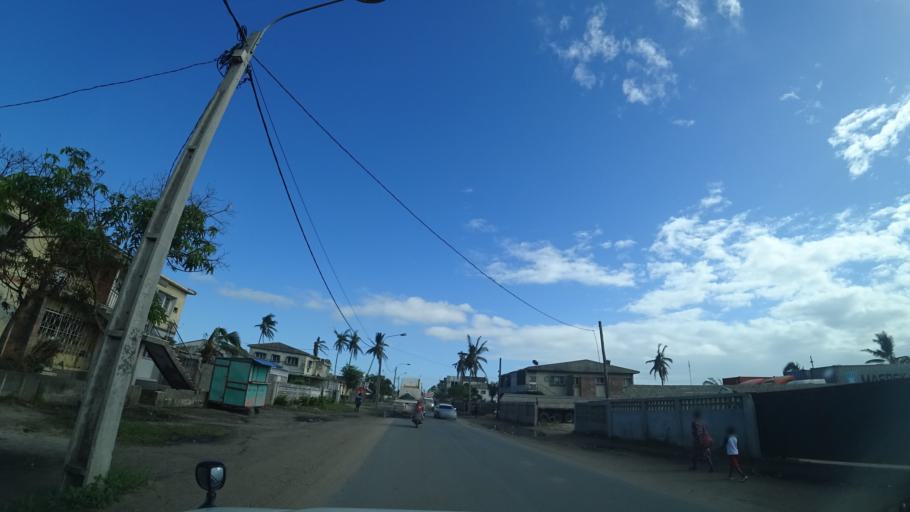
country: MZ
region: Sofala
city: Beira
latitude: -19.7854
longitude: 34.8813
